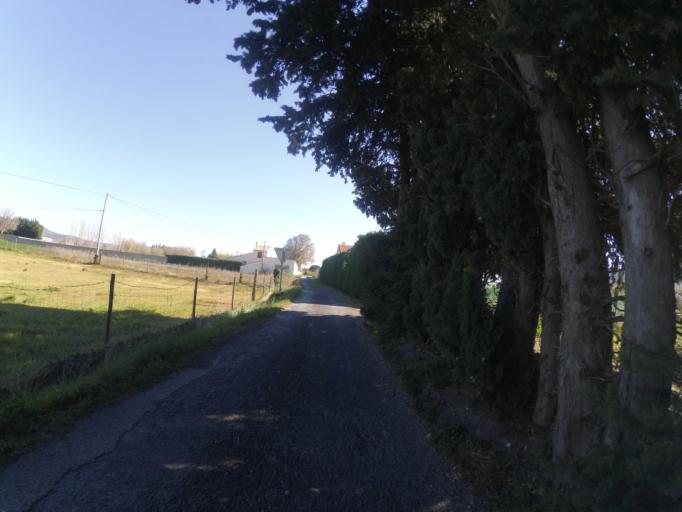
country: FR
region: Languedoc-Roussillon
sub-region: Departement des Pyrenees-Orientales
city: Ille-sur-Tet
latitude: 42.6601
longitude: 2.6218
